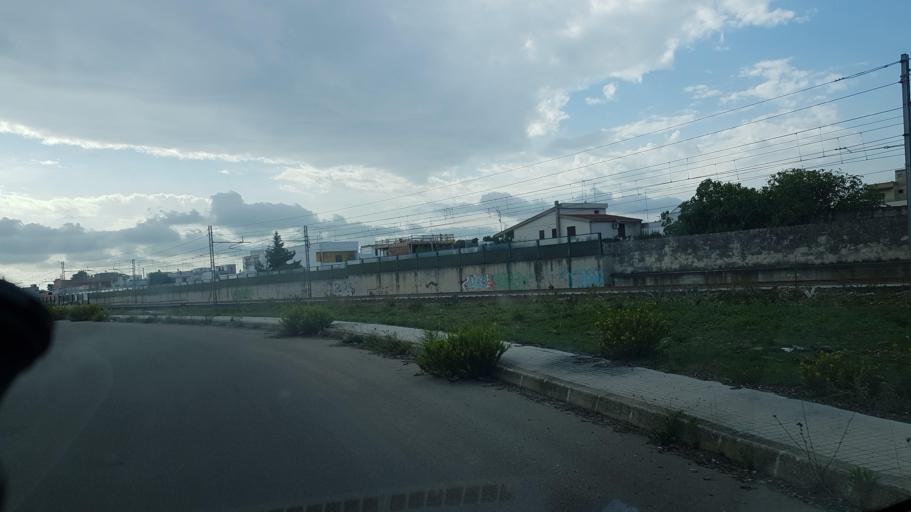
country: IT
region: Apulia
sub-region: Provincia di Brindisi
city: San Pietro Vernotico
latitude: 40.4825
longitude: 18.0056
